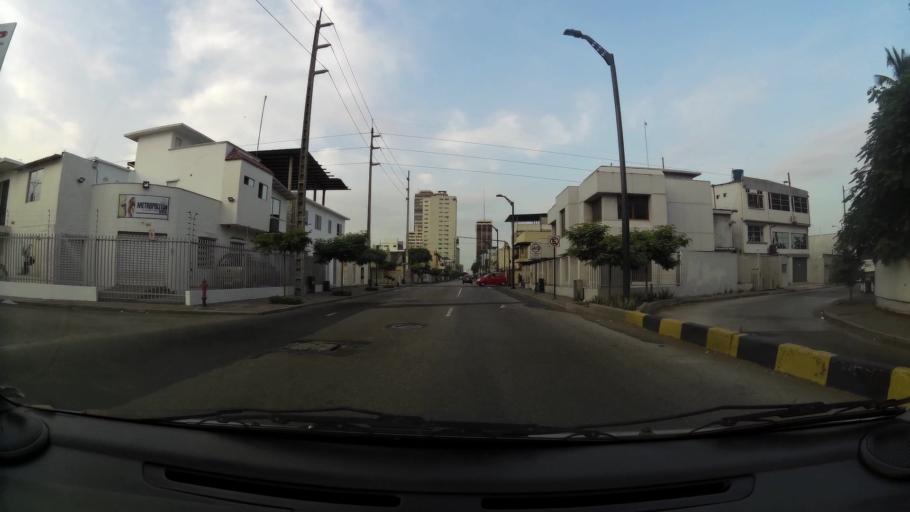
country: EC
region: Guayas
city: Guayaquil
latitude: -2.1839
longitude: -79.8928
